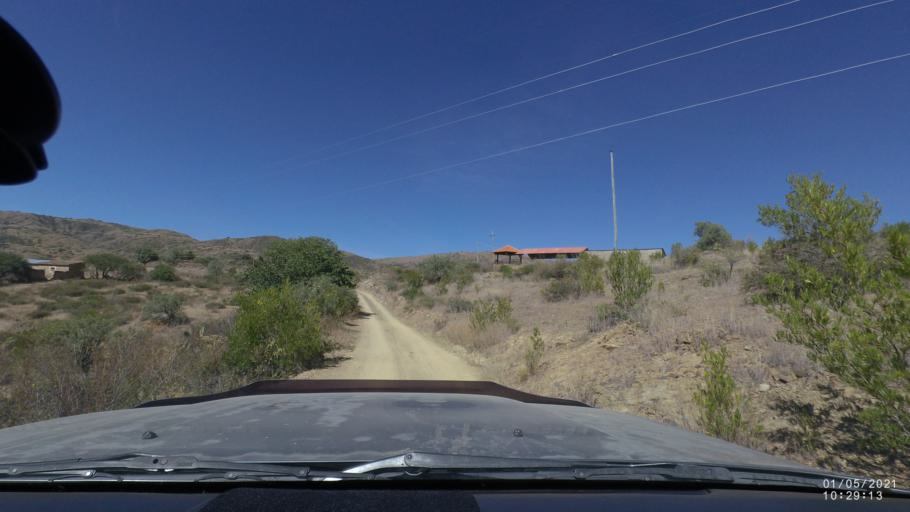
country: BO
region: Cochabamba
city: Capinota
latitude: -17.5923
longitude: -66.1902
